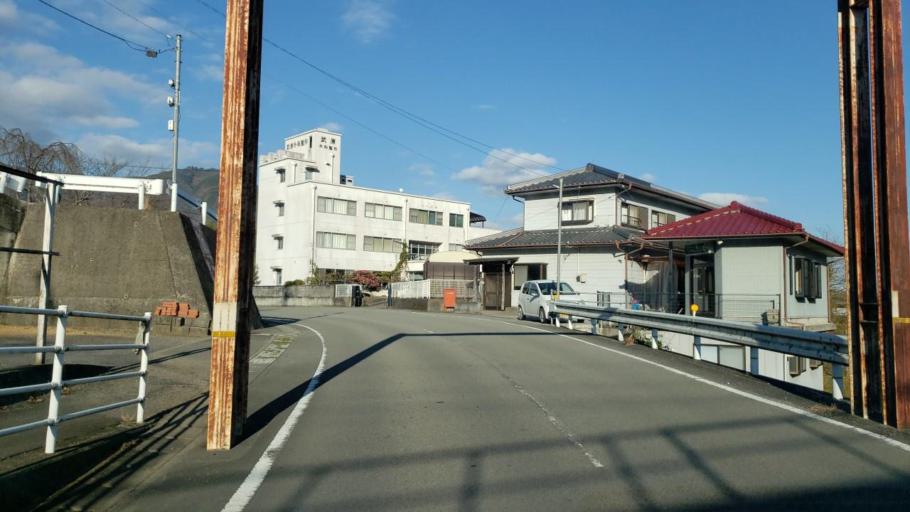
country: JP
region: Tokushima
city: Wakimachi
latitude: 34.0412
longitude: 134.0285
